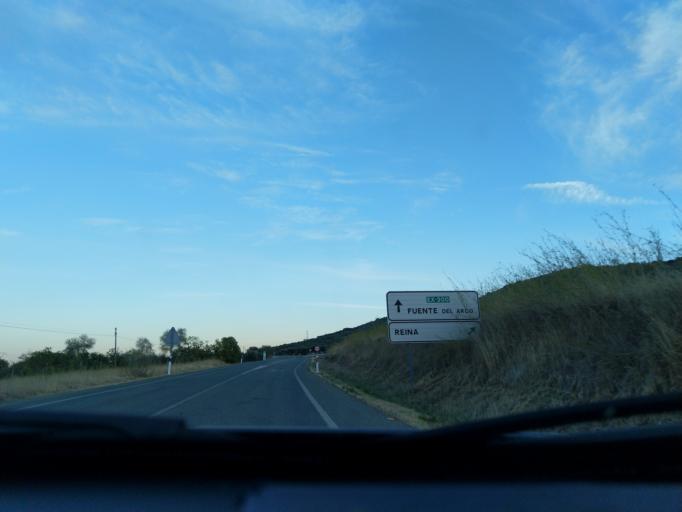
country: ES
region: Extremadura
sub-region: Provincia de Badajoz
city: Reina
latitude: 38.1904
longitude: -5.9465
